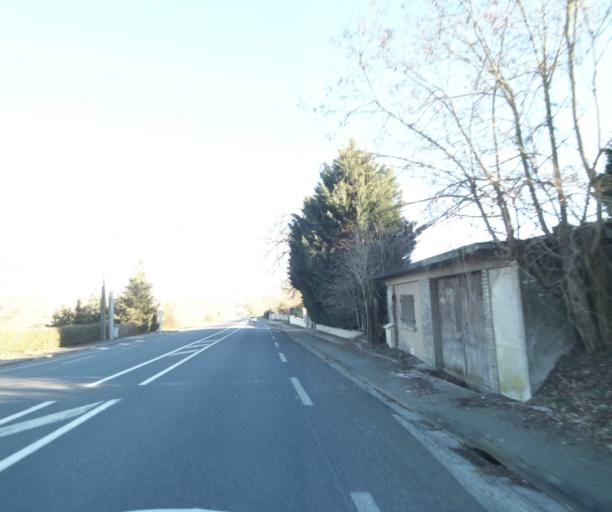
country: FR
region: Lorraine
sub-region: Departement de Meurthe-et-Moselle
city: Saint-Nicolas-de-Port
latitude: 48.6367
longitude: 6.2807
